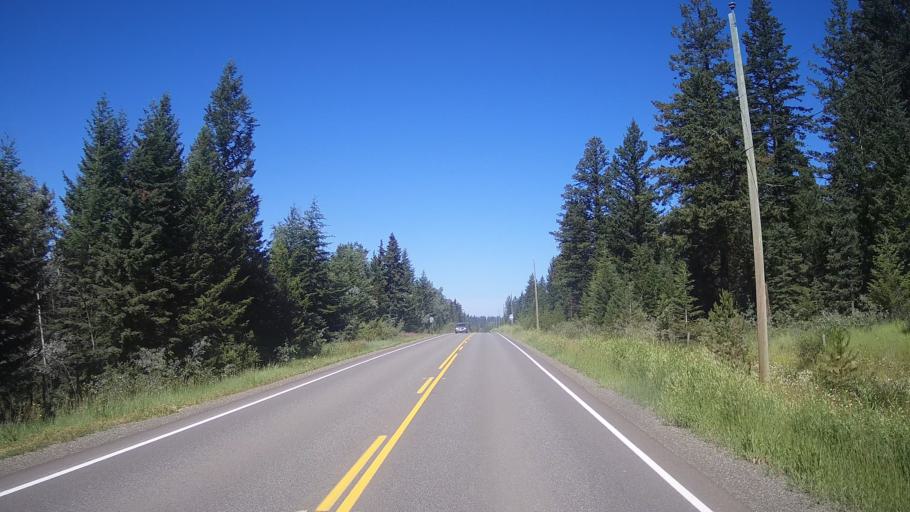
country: CA
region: British Columbia
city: Cache Creek
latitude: 51.5423
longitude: -121.0575
